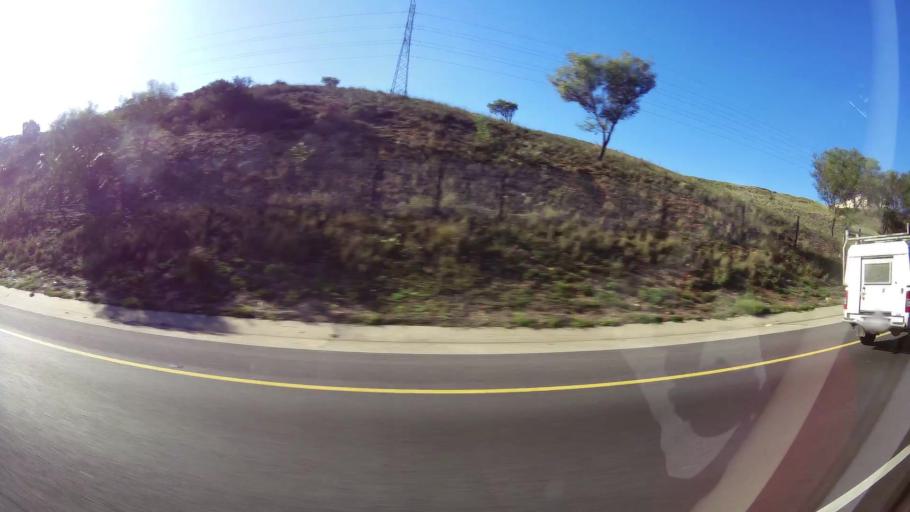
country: ZA
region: Eastern Cape
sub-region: Nelson Mandela Bay Metropolitan Municipality
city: Port Elizabeth
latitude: -33.9314
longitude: 25.5579
